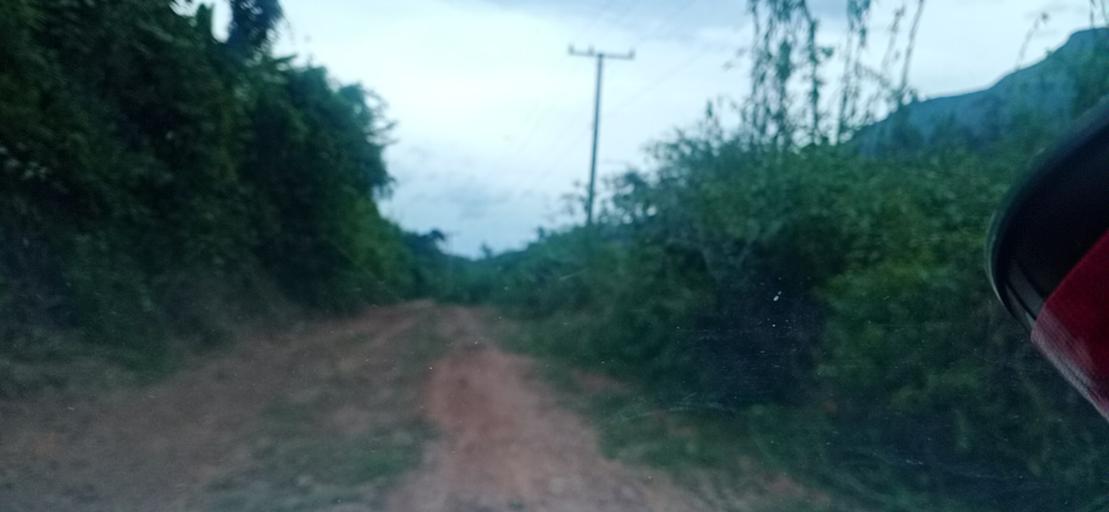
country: TH
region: Changwat Bueng Kan
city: Pak Khat
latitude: 18.5595
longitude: 103.2447
